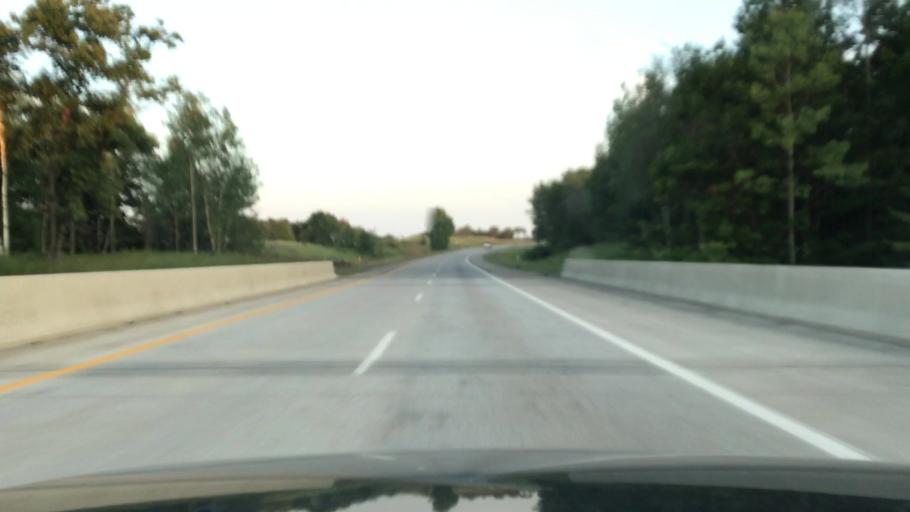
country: US
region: Michigan
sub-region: Montcalm County
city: Howard City
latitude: 43.4724
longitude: -85.4782
